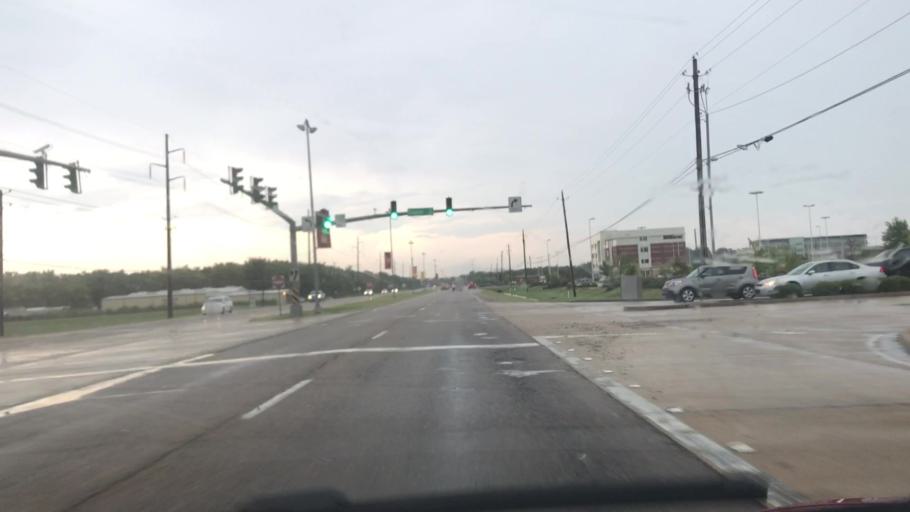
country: US
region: Louisiana
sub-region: Bossier Parish
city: Red Chute
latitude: 32.5409
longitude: -93.6488
